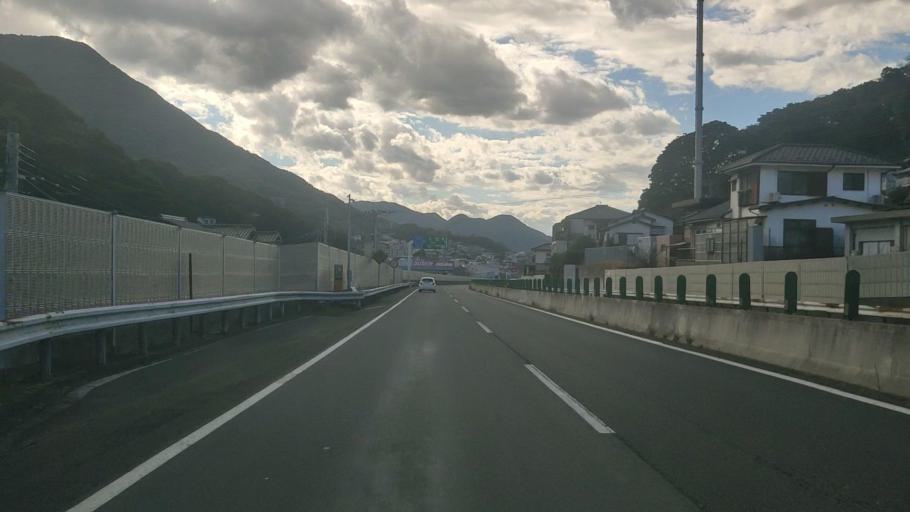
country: JP
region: Yamaguchi
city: Shimonoseki
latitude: 33.9109
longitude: 130.9573
